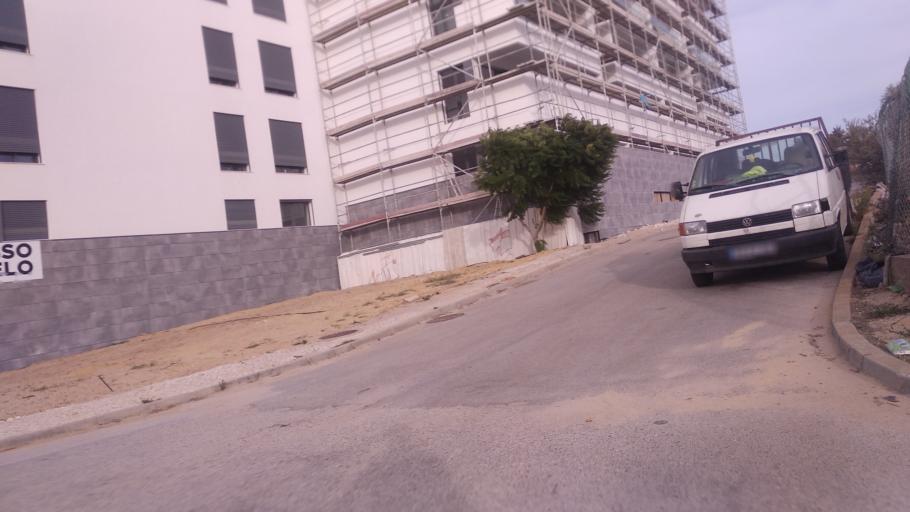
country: PT
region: Faro
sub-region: Faro
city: Faro
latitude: 37.0297
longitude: -7.9396
